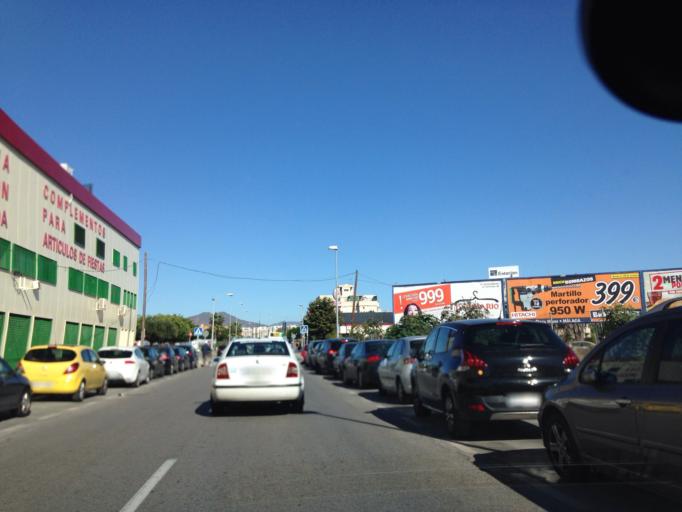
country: ES
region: Andalusia
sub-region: Provincia de Malaga
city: Malaga
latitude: 36.6855
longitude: -4.4576
